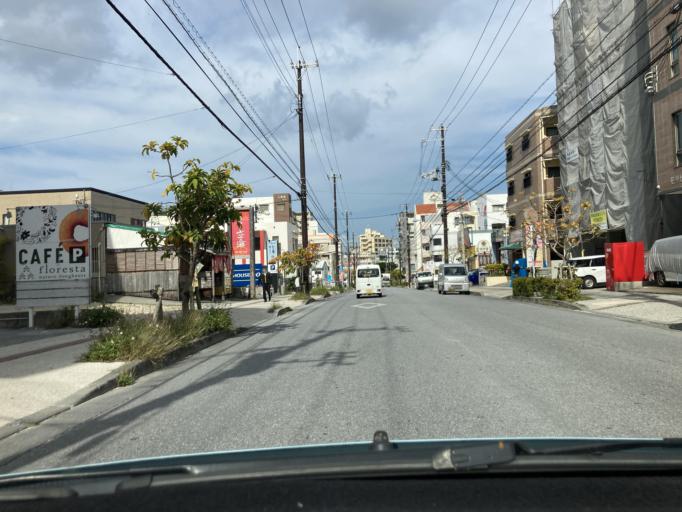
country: JP
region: Okinawa
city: Naha-shi
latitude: 26.2350
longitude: 127.6891
